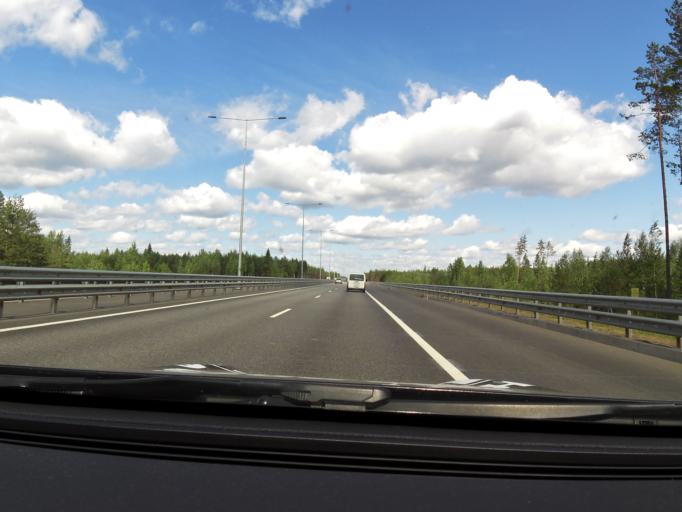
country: RU
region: Tverskaya
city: Krasnomayskiy
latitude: 57.5612
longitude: 34.2653
